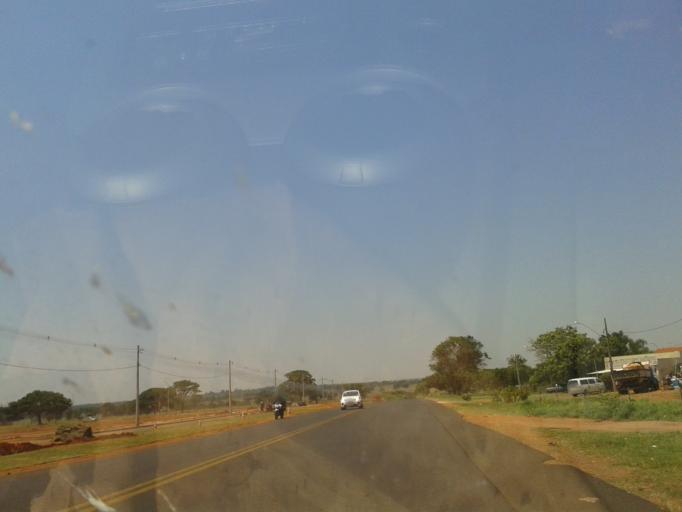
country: BR
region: Minas Gerais
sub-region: Uberlandia
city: Uberlandia
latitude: -18.9590
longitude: -48.3068
